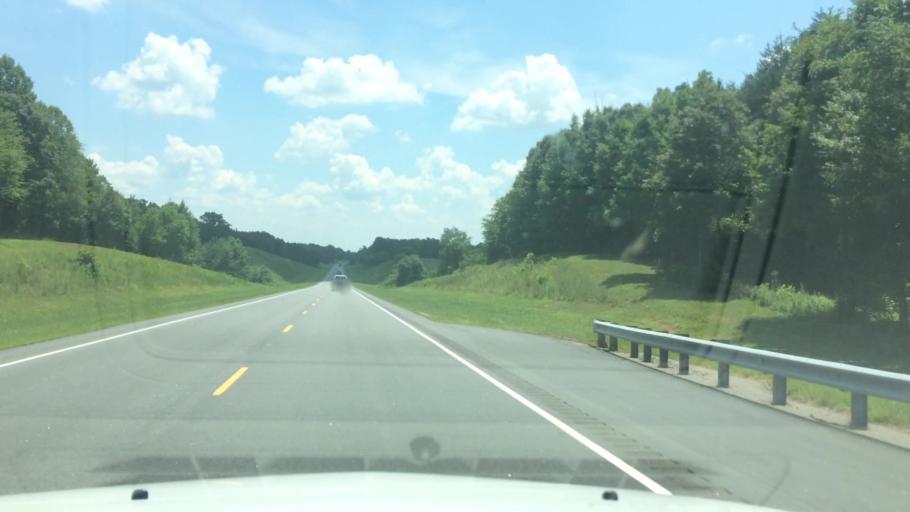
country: US
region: North Carolina
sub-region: Alexander County
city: Stony Point
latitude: 35.8829
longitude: -81.0747
